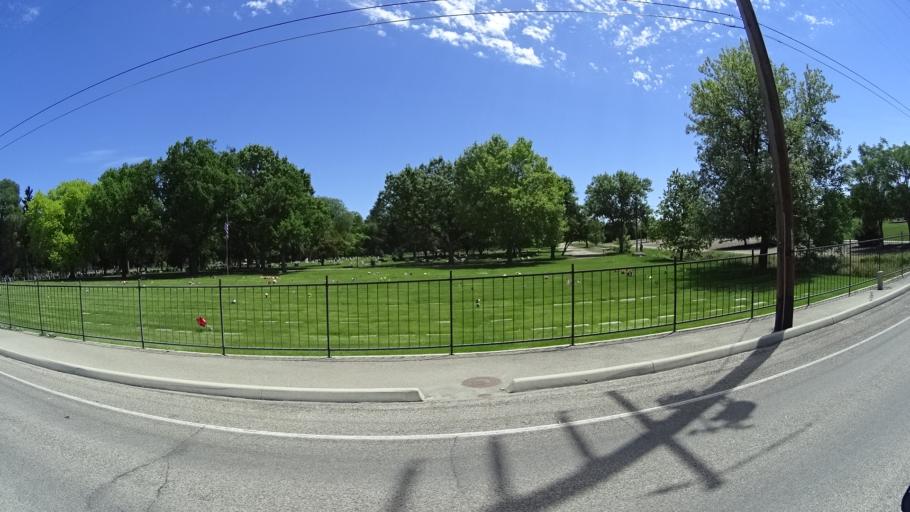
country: US
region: Idaho
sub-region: Ada County
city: Garden City
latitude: 43.6067
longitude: -116.2338
